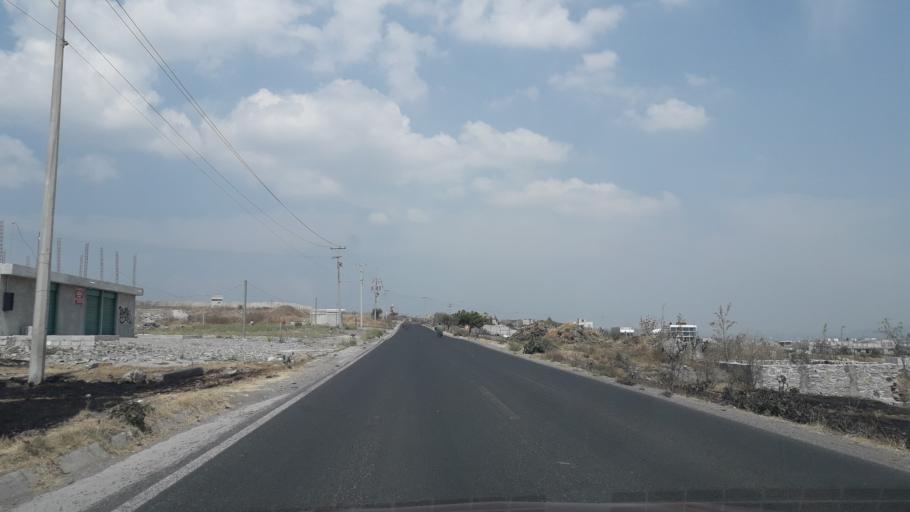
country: MX
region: Puebla
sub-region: Puebla
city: El Capulo (La Quebradora)
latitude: 18.9360
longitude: -98.2681
